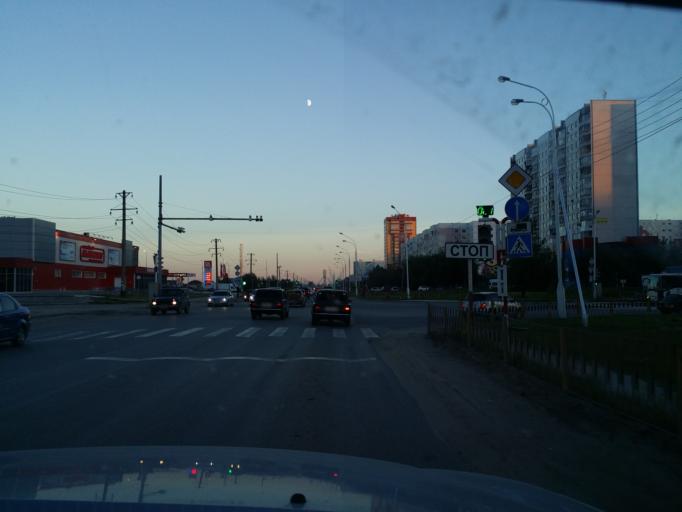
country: RU
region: Khanty-Mansiyskiy Avtonomnyy Okrug
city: Nizhnevartovsk
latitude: 60.9306
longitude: 76.6083
